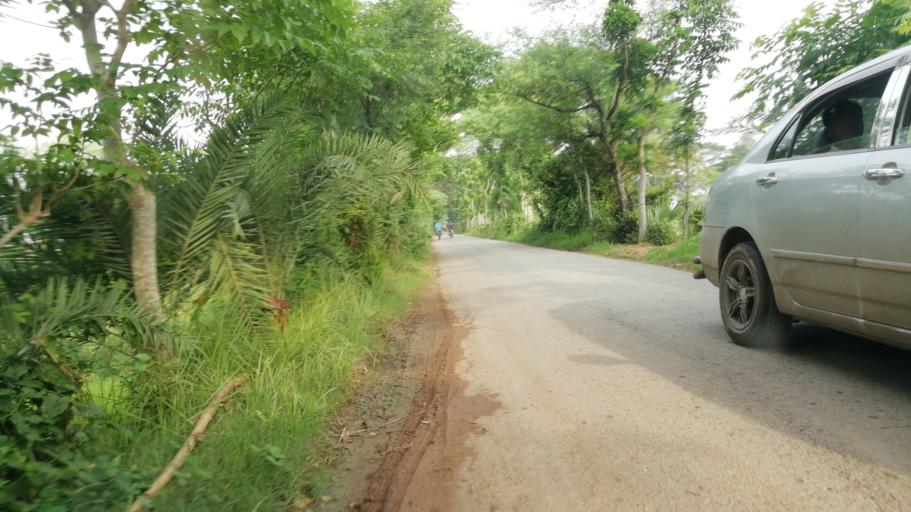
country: BD
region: Khulna
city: Bhatpara Abhaynagar
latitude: 23.0400
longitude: 89.3222
